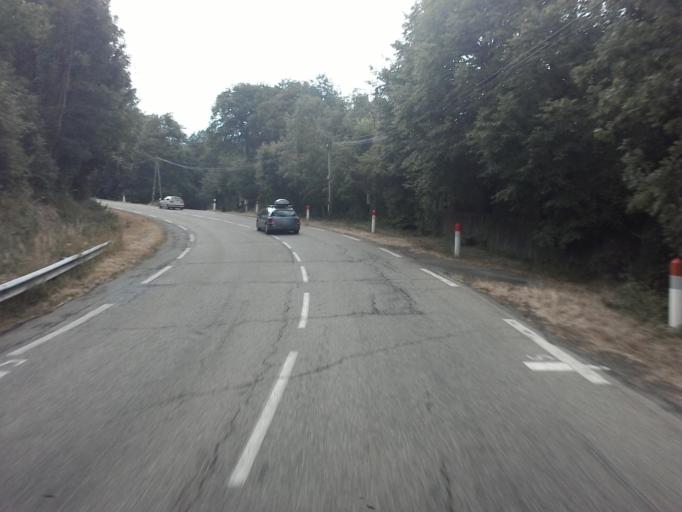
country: FR
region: Provence-Alpes-Cote d'Azur
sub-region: Departement des Hautes-Alpes
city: Saint-Bonnet-en-Champsaur
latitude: 44.7781
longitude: 5.9856
